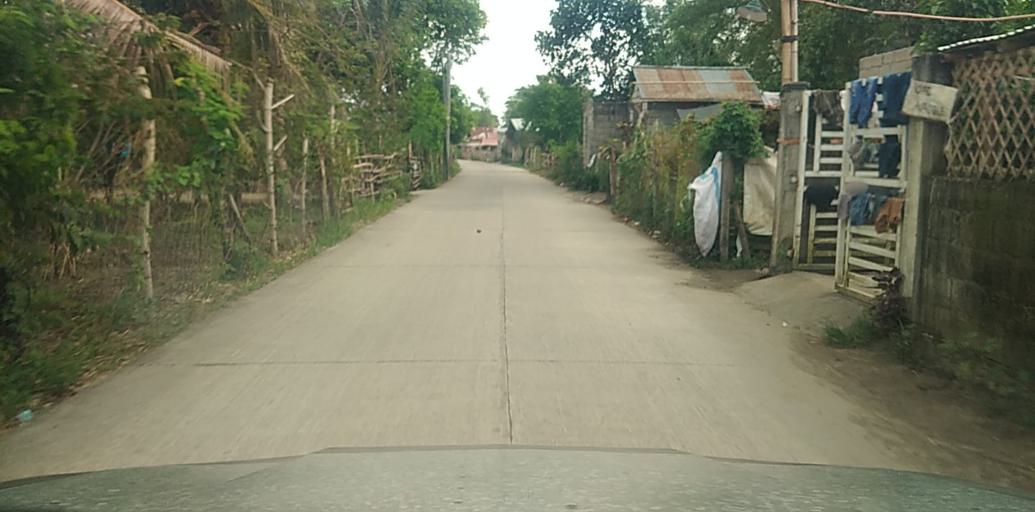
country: PH
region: Central Luzon
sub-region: Province of Pampanga
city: Panlinlang
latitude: 15.1821
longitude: 120.6983
